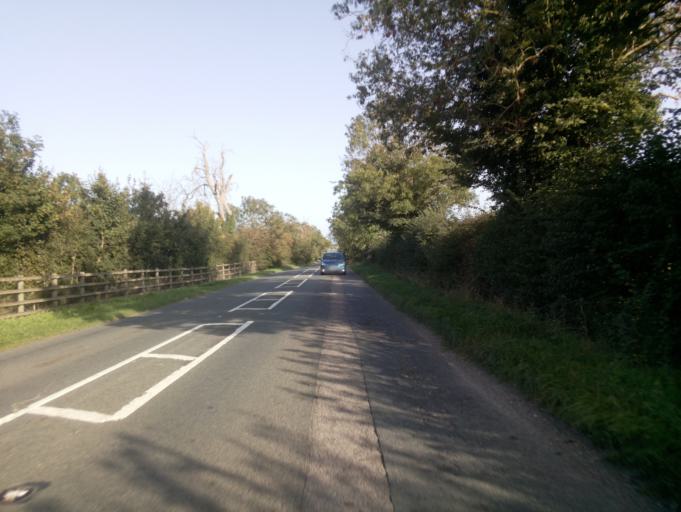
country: GB
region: England
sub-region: Gloucestershire
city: Gloucester
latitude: 51.9615
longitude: -2.2633
